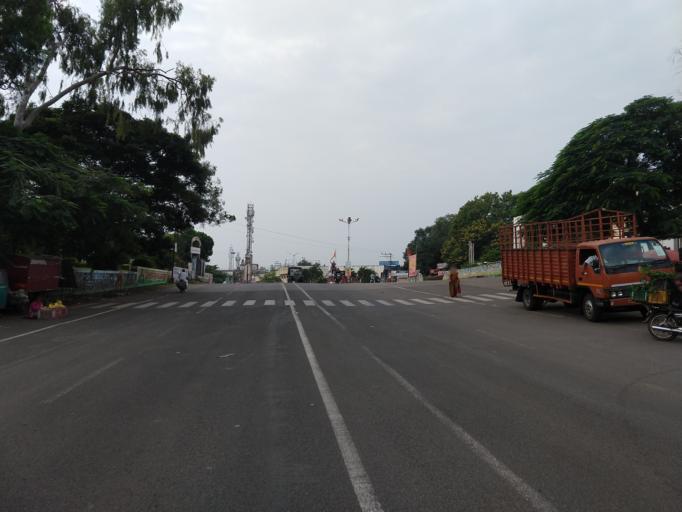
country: IN
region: Maharashtra
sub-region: Pune Division
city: Sasvad
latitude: 18.3483
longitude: 74.0288
